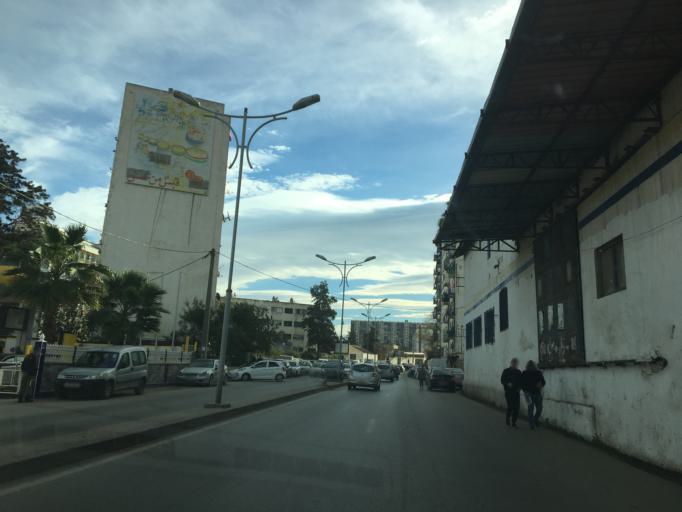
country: DZ
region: Alger
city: Birkhadem
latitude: 36.7405
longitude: 3.0893
